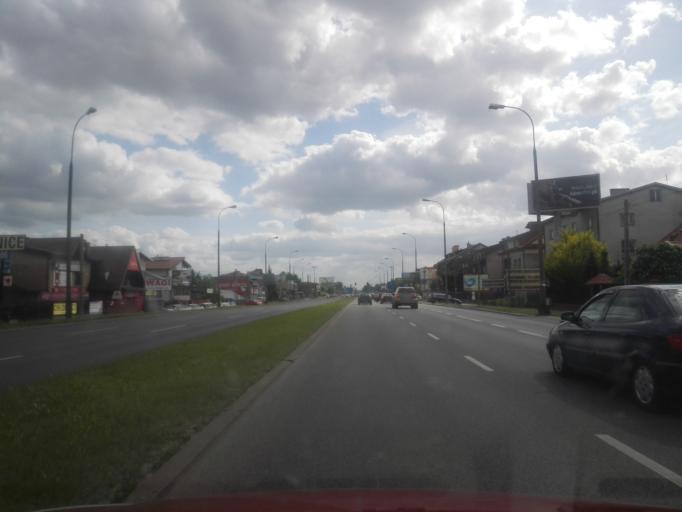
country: PL
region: Masovian Voivodeship
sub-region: Warszawa
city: Targowek
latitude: 52.2826
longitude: 21.0718
